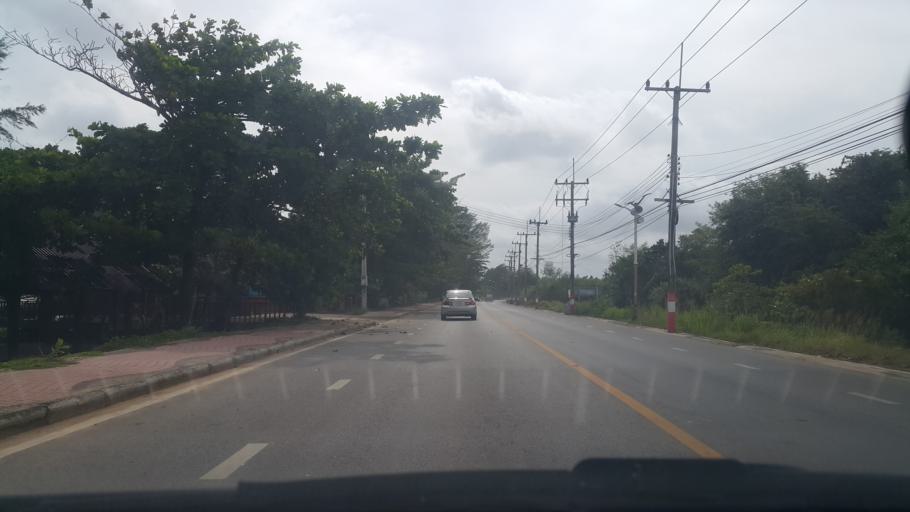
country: TH
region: Rayong
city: Rayong
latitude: 12.6305
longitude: 101.3457
